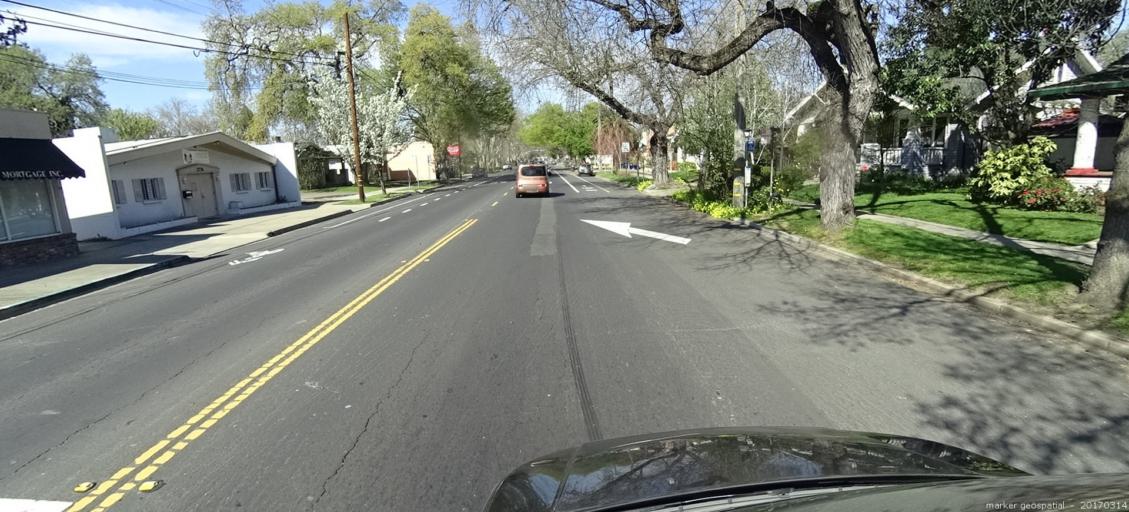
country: US
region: California
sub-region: Sacramento County
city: Sacramento
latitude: 38.5533
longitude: -121.4880
